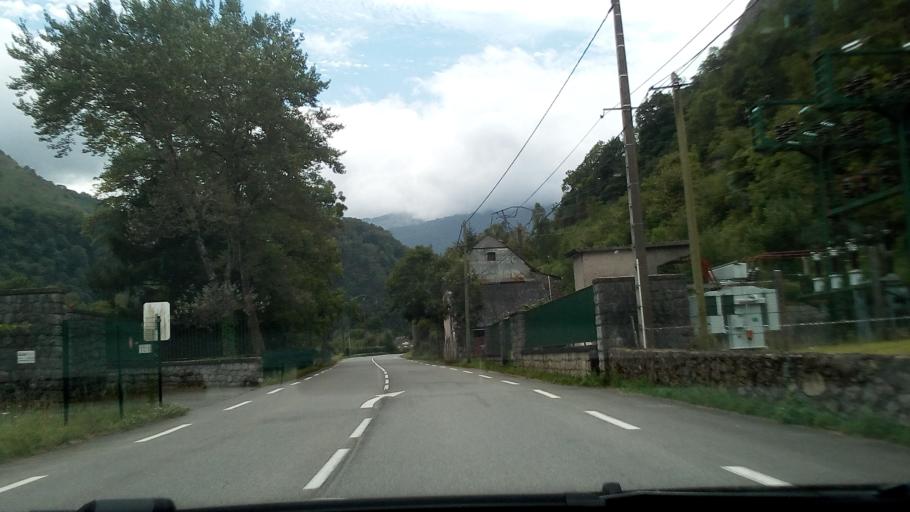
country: FR
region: Aquitaine
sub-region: Departement des Pyrenees-Atlantiques
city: Laruns
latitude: 43.0100
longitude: -0.4221
